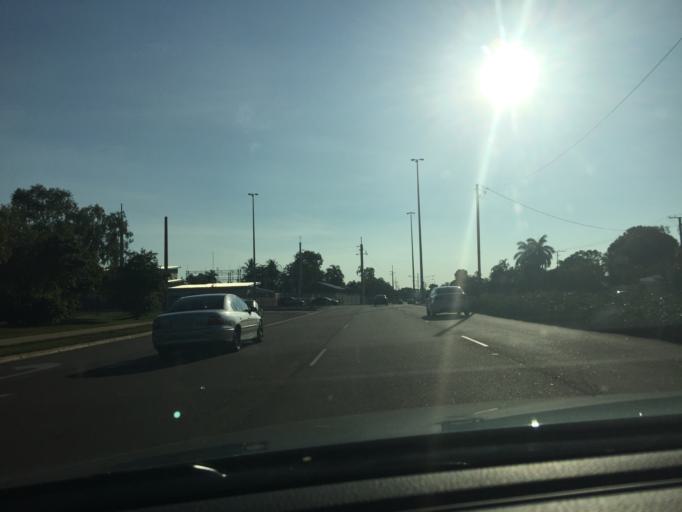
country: AU
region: Northern Territory
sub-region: Darwin
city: Nightcliff
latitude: -12.3826
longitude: 130.8775
